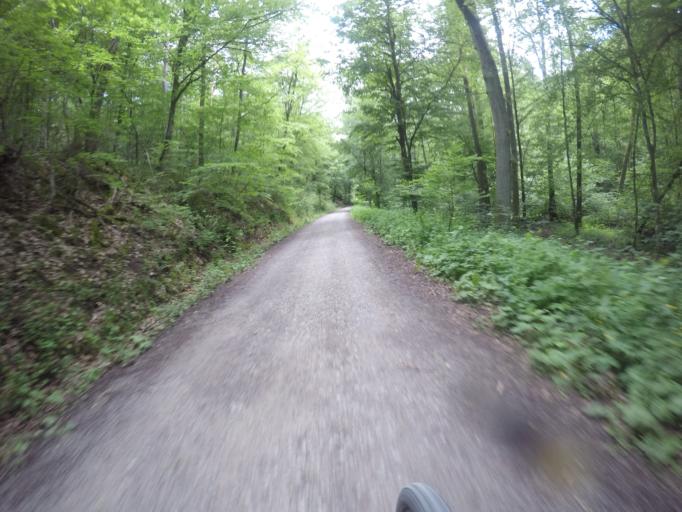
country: DE
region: Baden-Wuerttemberg
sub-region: Regierungsbezirk Stuttgart
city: Nufringen
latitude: 48.5975
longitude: 8.9227
